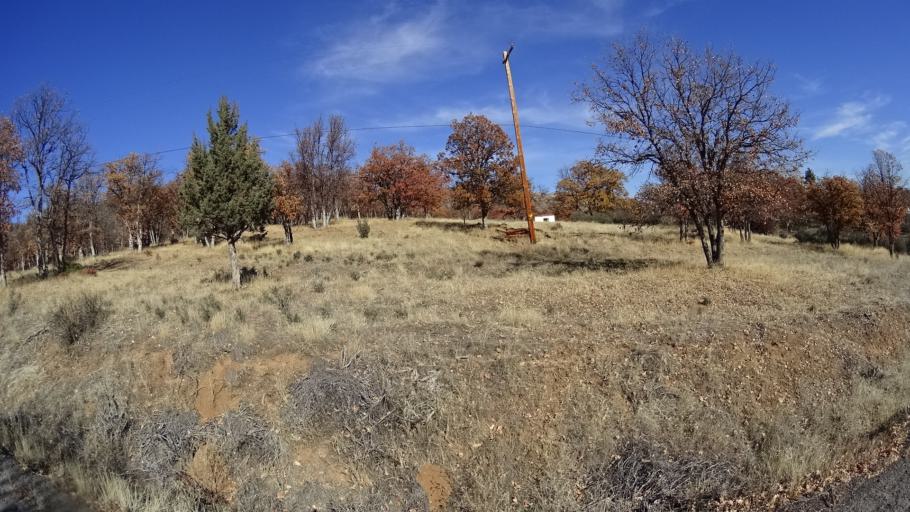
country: US
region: California
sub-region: Siskiyou County
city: Yreka
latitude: 41.7715
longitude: -122.6416
